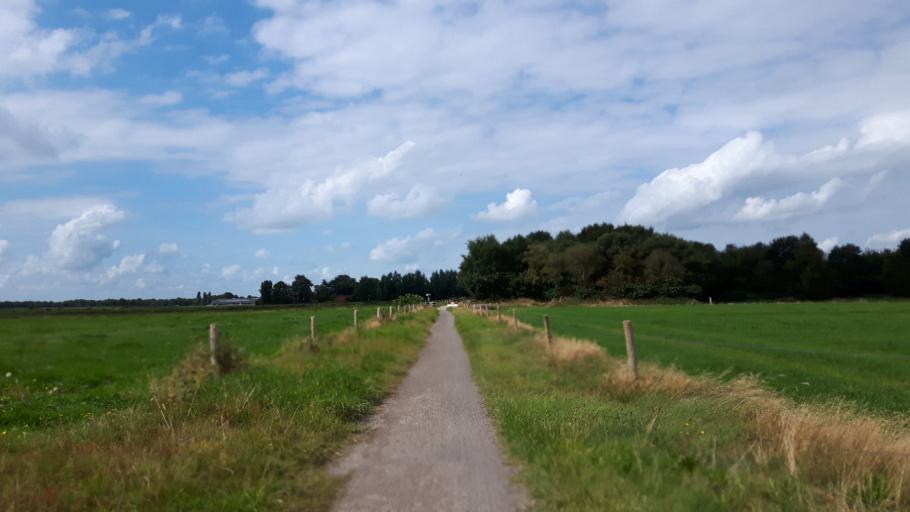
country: NL
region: Groningen
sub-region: Gemeente Leek
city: Leek
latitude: 53.0817
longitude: 6.3281
